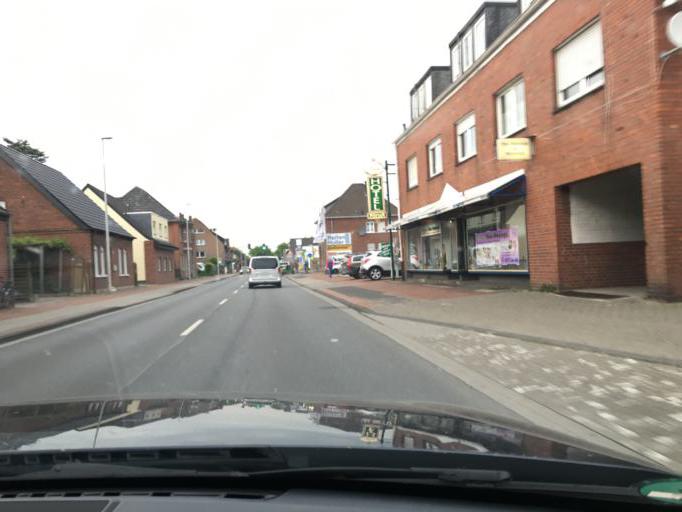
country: DE
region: North Rhine-Westphalia
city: Emsdetten
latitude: 52.1692
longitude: 7.5403
